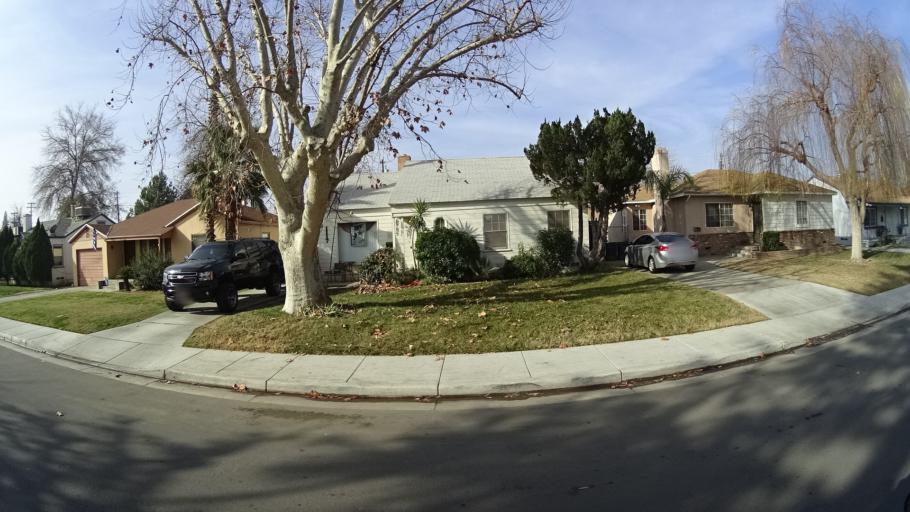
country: US
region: California
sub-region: Kern County
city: Bakersfield
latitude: 35.3441
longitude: -119.0201
